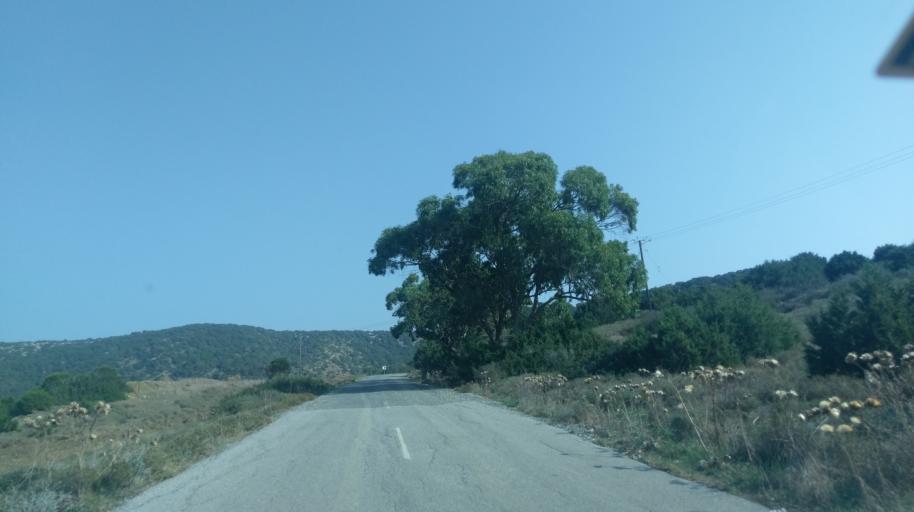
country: CY
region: Ammochostos
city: Rizokarpaso
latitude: 35.6479
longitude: 34.5458
